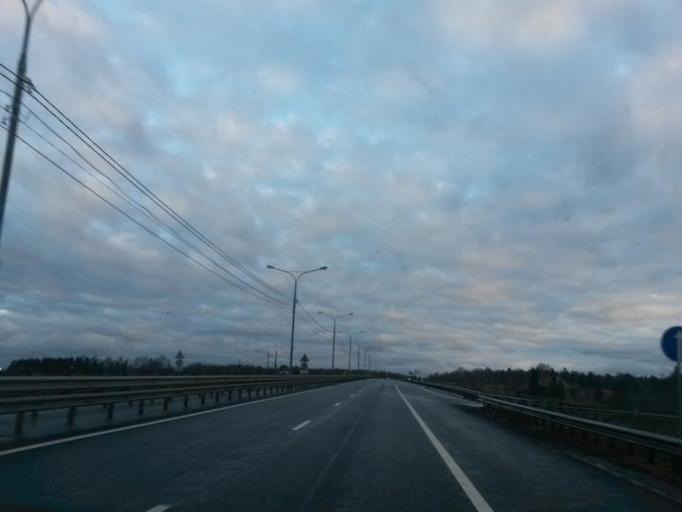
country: RU
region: Moskovskaya
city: Svatkovo
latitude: 56.3359
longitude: 38.2600
